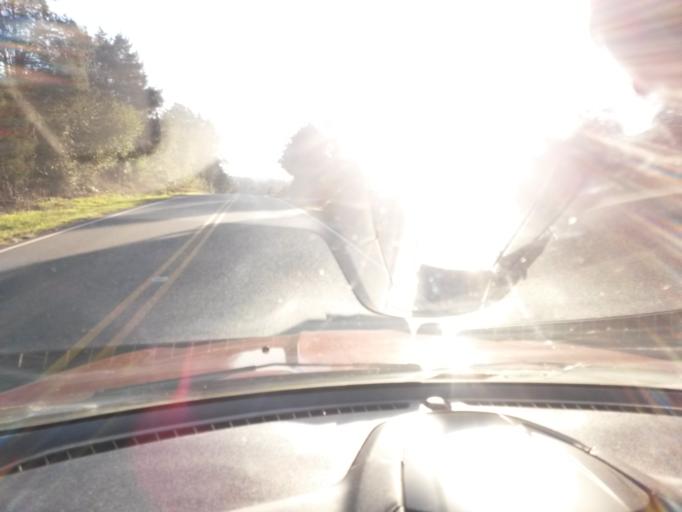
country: US
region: Virginia
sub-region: Amherst County
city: Amherst
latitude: 37.6037
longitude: -79.0708
